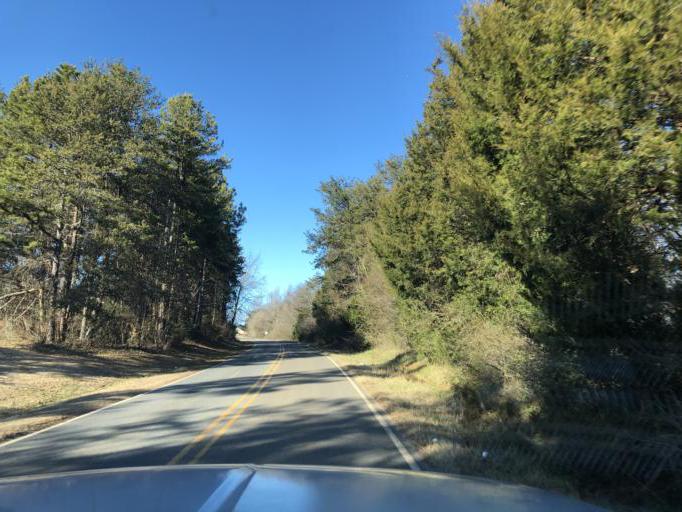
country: US
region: North Carolina
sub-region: Cleveland County
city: Shelby
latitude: 35.3339
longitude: -81.5393
